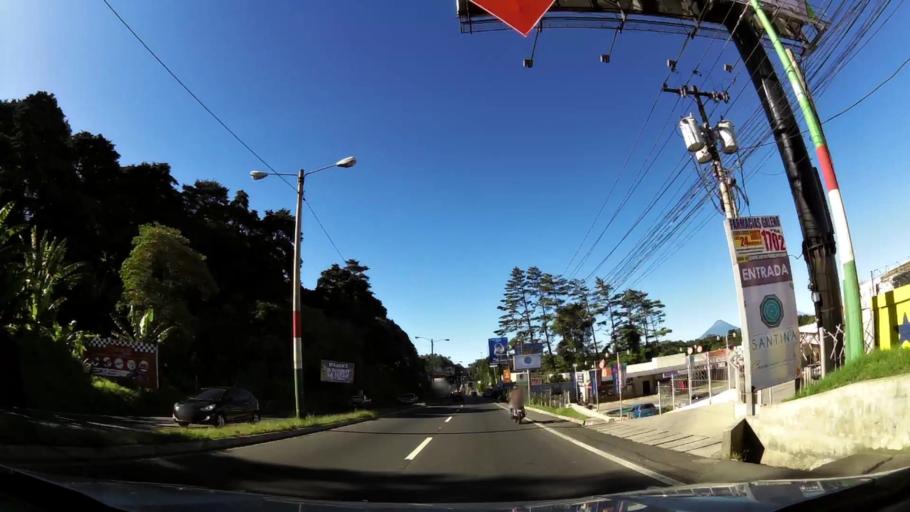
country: GT
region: Guatemala
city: San Jose Pinula
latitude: 14.5350
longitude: -90.4592
